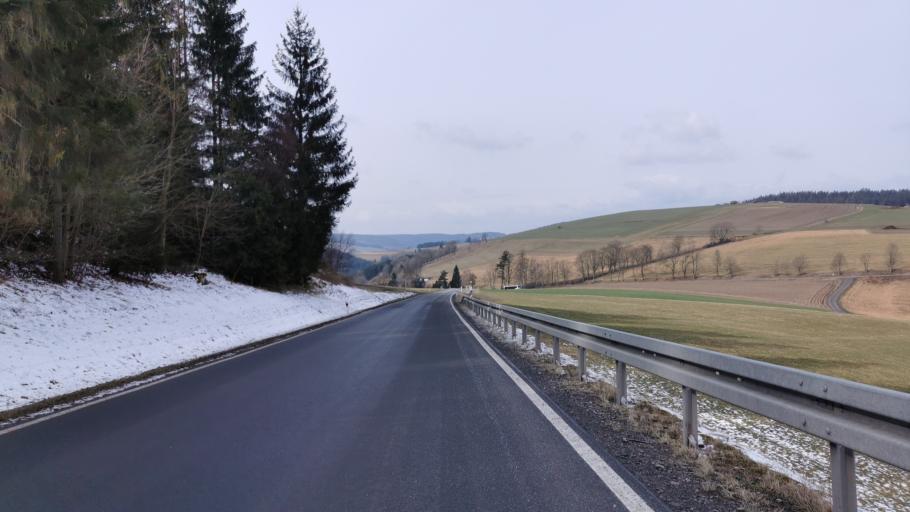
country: DE
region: Bavaria
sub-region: Upper Franconia
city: Ludwigsstadt
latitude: 50.4965
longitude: 11.3982
